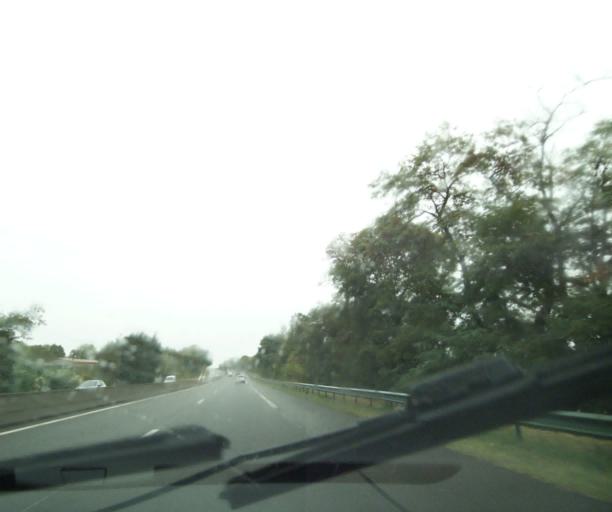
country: FR
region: Auvergne
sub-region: Departement du Puy-de-Dome
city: Menetrol
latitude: 45.8631
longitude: 3.1188
